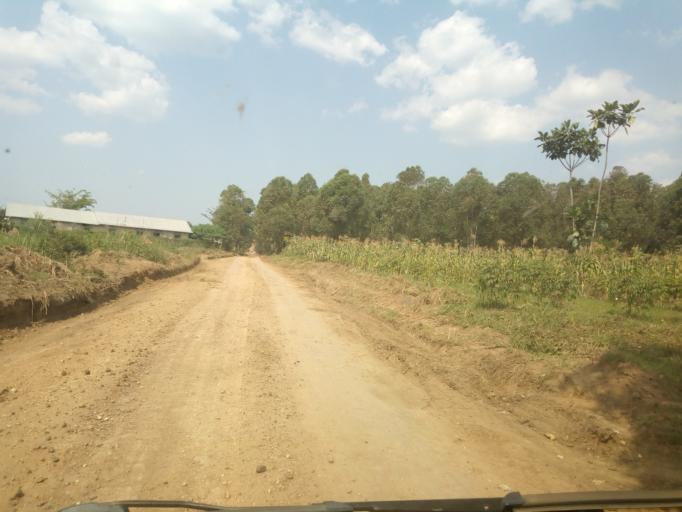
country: UG
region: Western Region
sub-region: Kanungu District
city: Ntungamo
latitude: -0.7834
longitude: 29.6963
